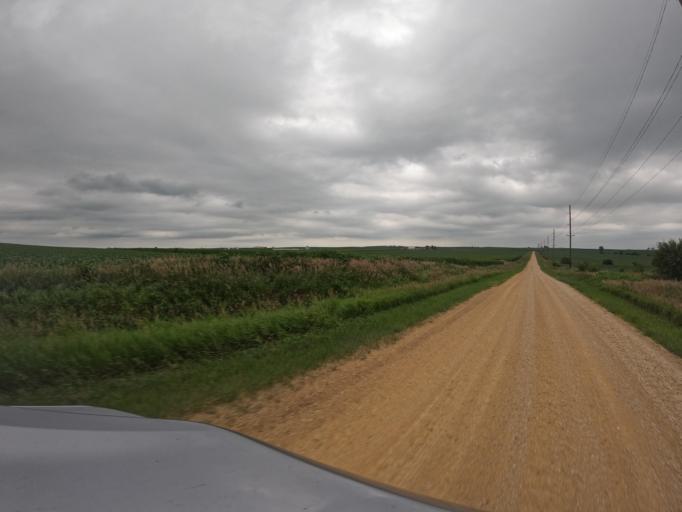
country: US
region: Iowa
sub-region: Clinton County
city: De Witt
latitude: 41.9383
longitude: -90.5972
